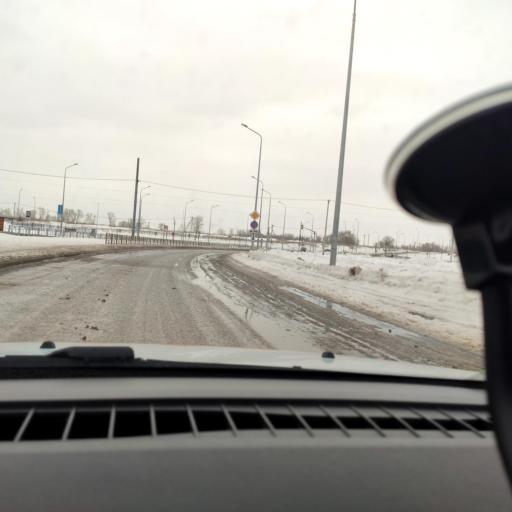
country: RU
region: Samara
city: Samara
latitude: 53.0974
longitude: 50.1738
